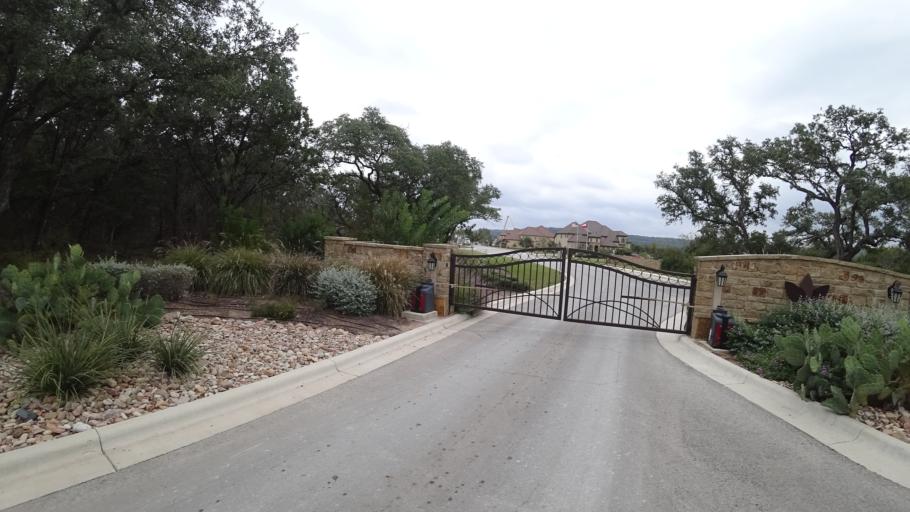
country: US
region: Texas
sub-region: Travis County
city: Bee Cave
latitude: 30.3364
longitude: -97.9200
